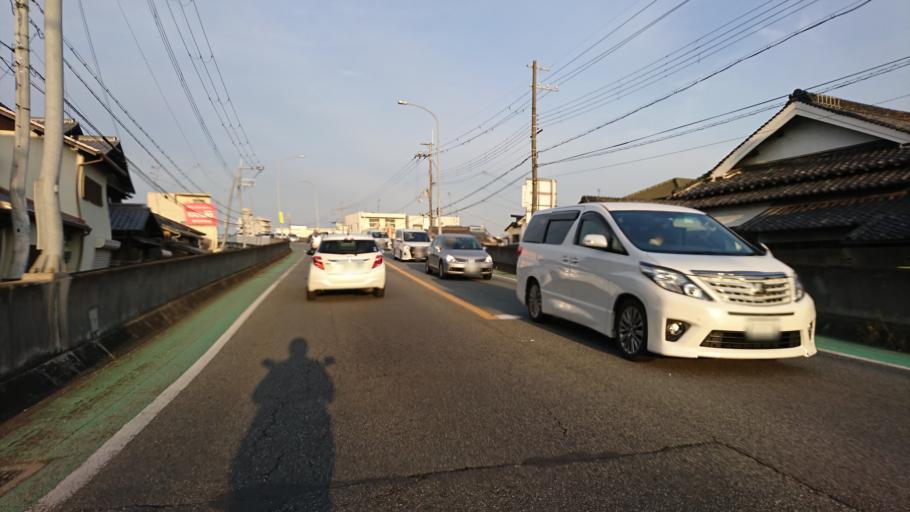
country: JP
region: Hyogo
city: Kakogawacho-honmachi
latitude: 34.7473
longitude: 134.8654
